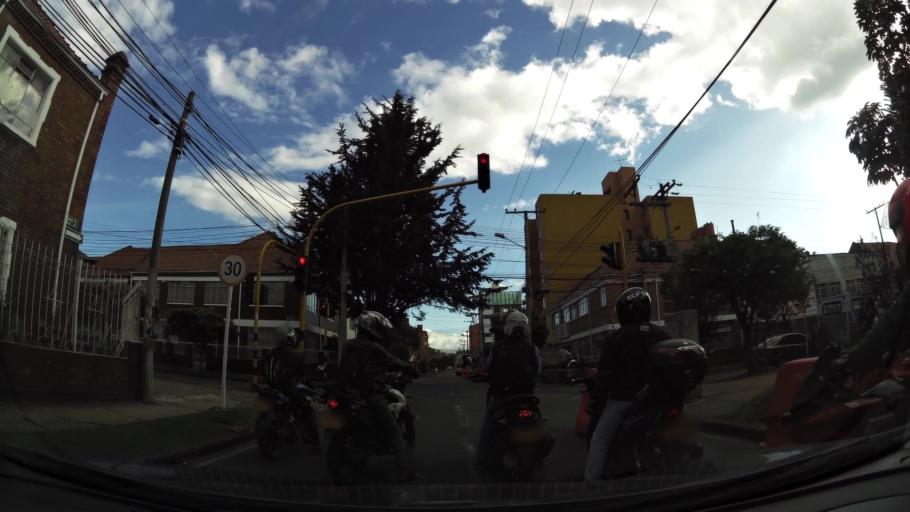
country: CO
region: Bogota D.C.
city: Bogota
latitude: 4.6479
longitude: -74.0687
